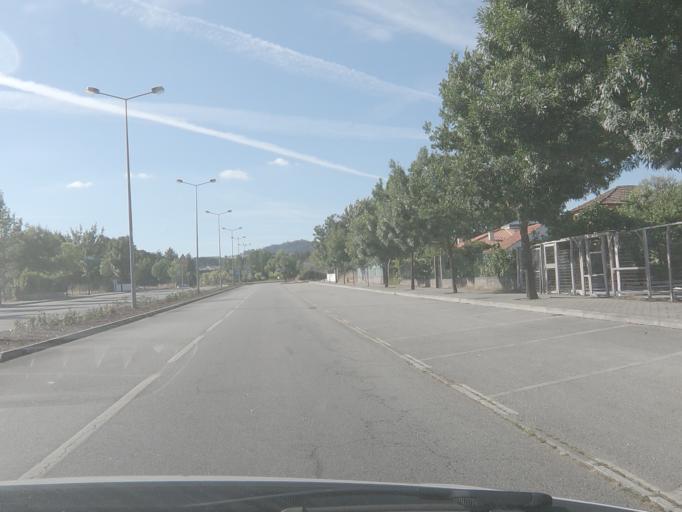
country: PT
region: Viseu
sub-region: Viseu
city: Viseu
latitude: 40.6705
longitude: -7.9044
